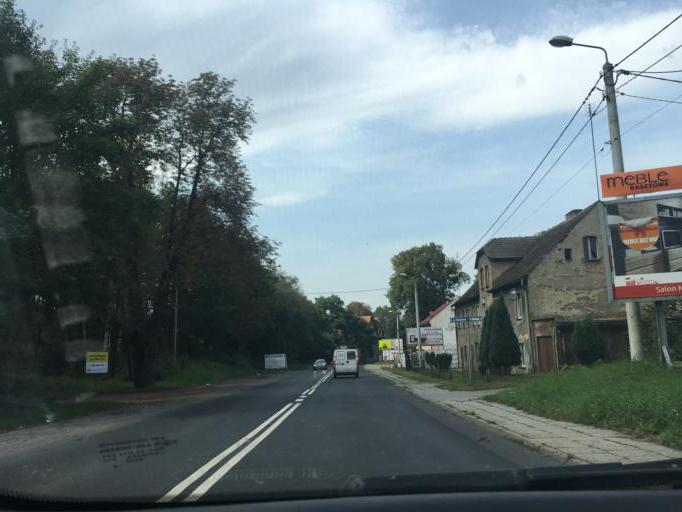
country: PL
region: Silesian Voivodeship
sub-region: Powiat raciborski
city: Pogrzebien
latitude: 50.0863
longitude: 18.2613
